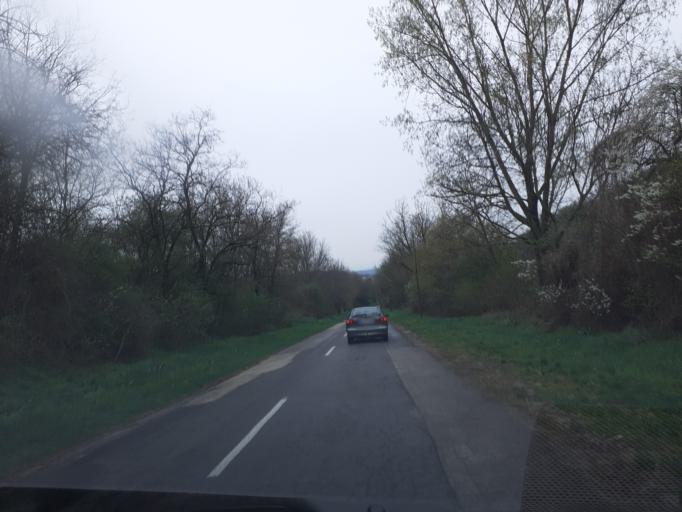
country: HU
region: Tolna
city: Hogyesz
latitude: 46.4290
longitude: 18.4506
